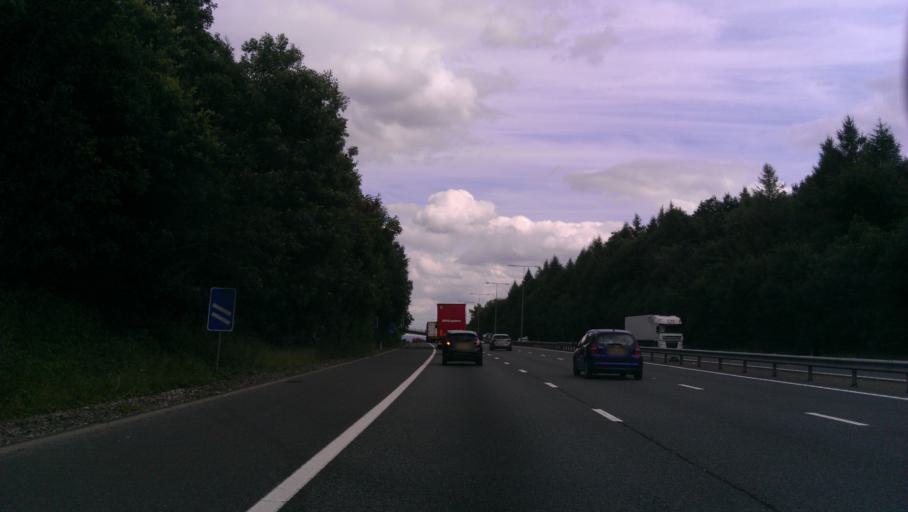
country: GB
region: England
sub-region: Kent
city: Borough Green
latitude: 51.3198
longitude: 0.2826
